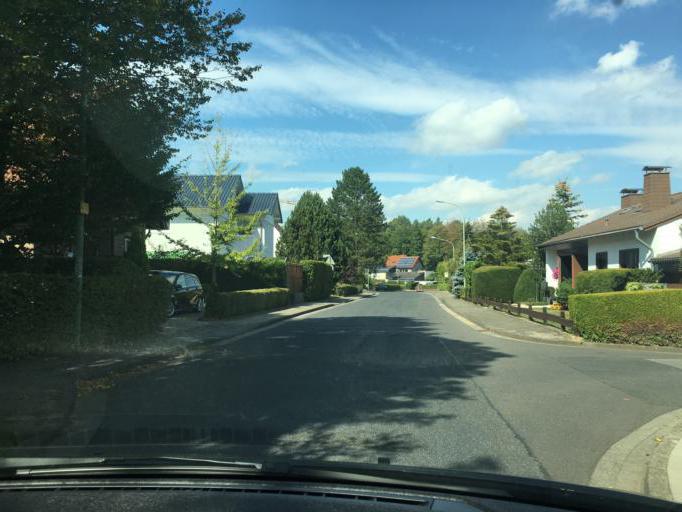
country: DE
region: North Rhine-Westphalia
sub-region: Regierungsbezirk Koln
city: Nideggen
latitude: 50.7011
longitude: 6.4702
